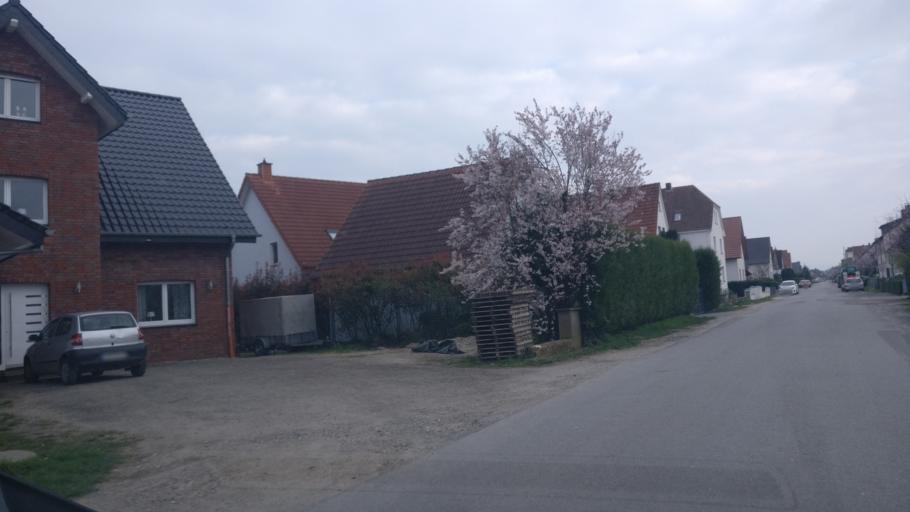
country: DE
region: North Rhine-Westphalia
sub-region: Regierungsbezirk Detmold
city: Lage
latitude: 52.0246
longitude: 8.7640
